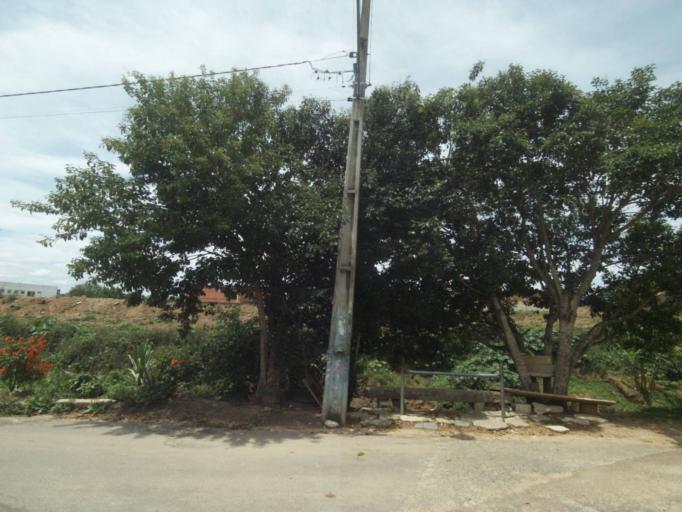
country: BR
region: Parana
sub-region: Curitiba
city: Curitiba
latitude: -25.4969
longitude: -49.3405
